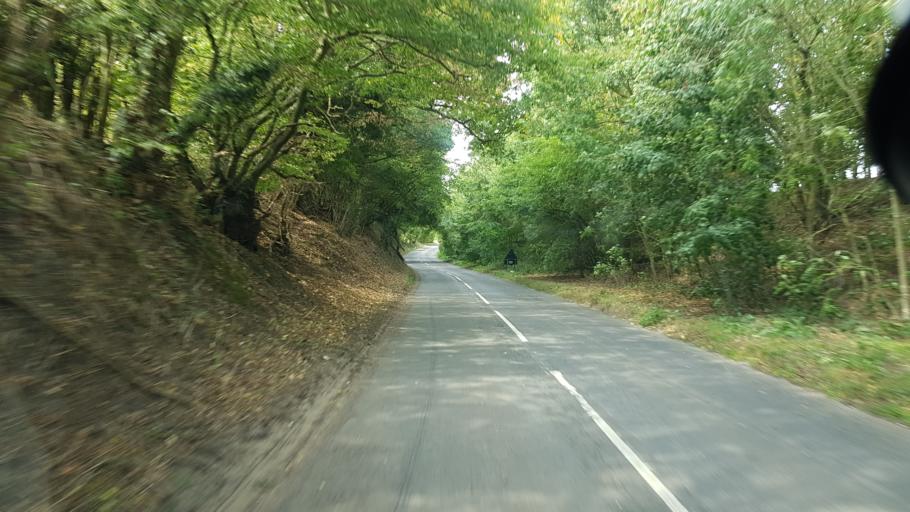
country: GB
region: England
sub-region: Kent
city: West Malling
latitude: 51.3121
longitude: 0.3636
